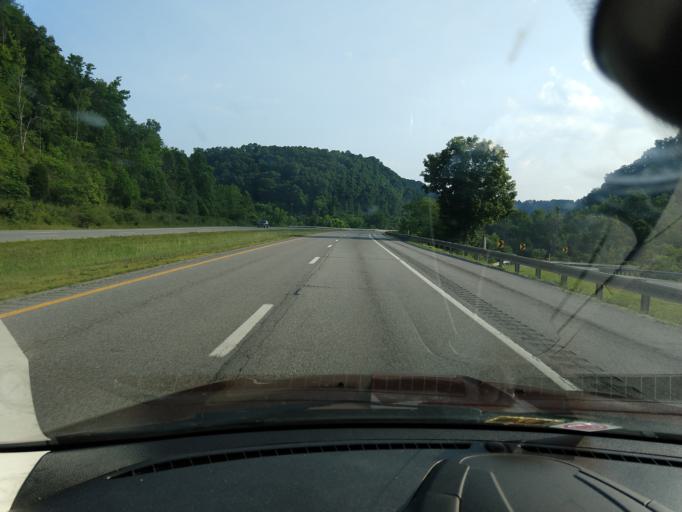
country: US
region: West Virginia
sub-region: Kanawha County
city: Sissonville
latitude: 38.5959
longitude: -81.6403
